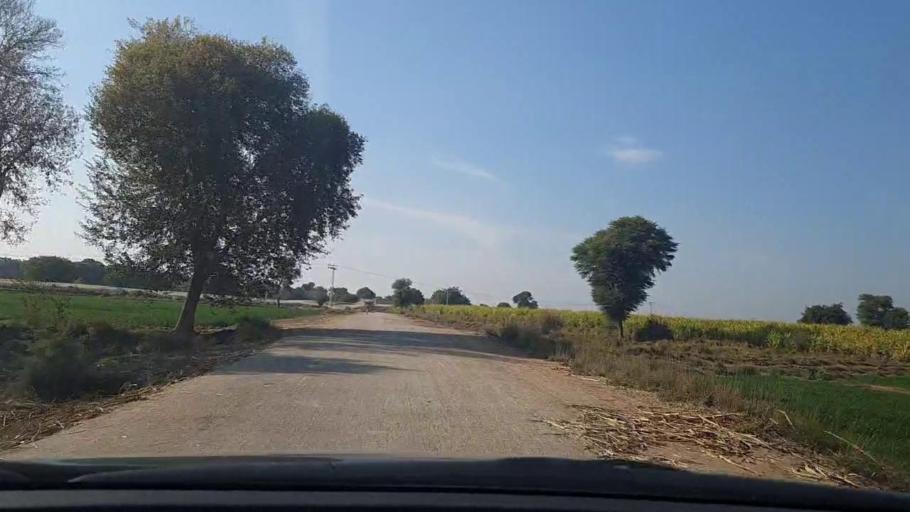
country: PK
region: Sindh
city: Sehwan
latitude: 26.3361
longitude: 67.9793
